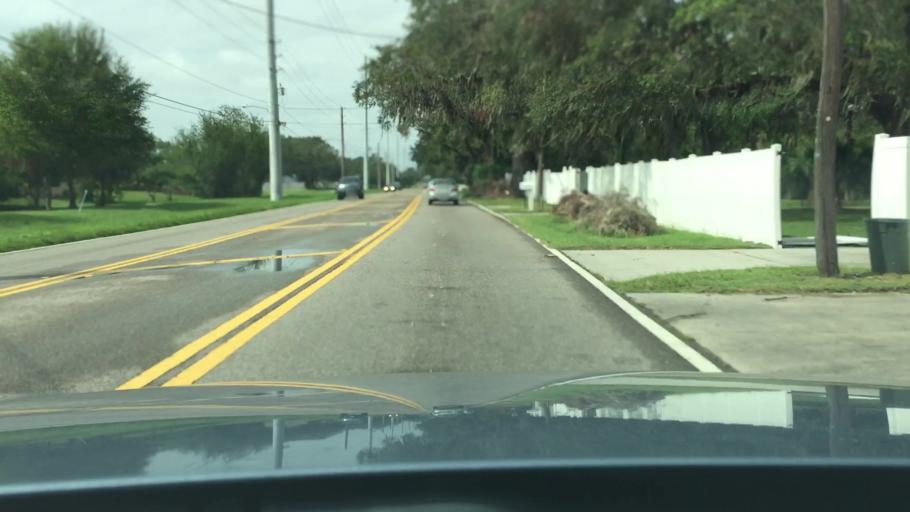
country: US
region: Florida
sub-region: Osceola County
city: Saint Cloud
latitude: 28.2655
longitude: -81.3472
